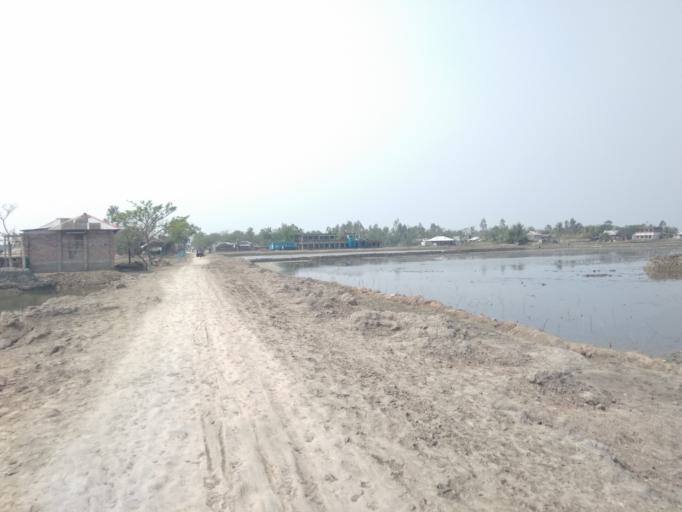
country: IN
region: West Bengal
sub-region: North 24 Parganas
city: Taki
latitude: 22.3478
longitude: 89.2216
